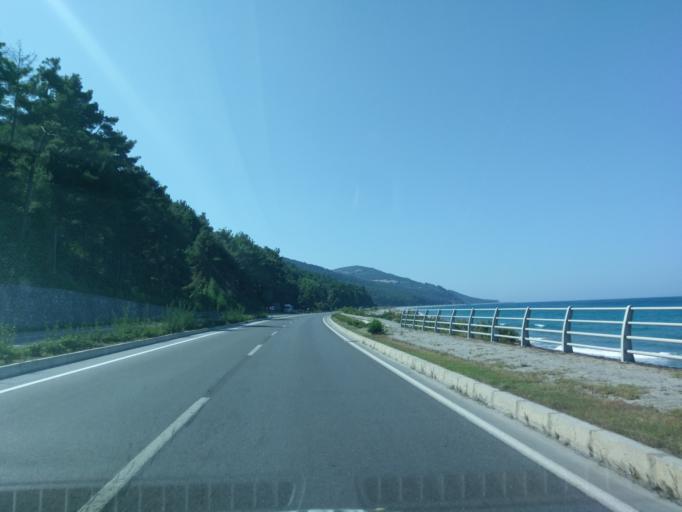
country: TR
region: Samsun
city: Yakakent
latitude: 41.6461
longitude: 35.4719
